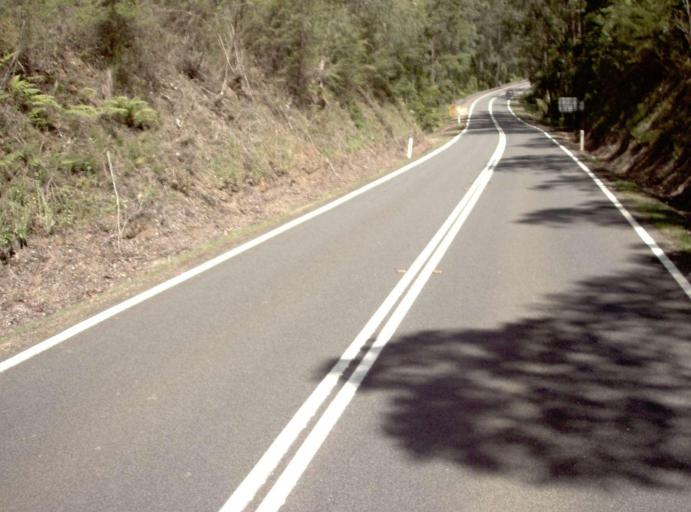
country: AU
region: New South Wales
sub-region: Bombala
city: Bombala
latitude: -37.5885
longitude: 148.9186
